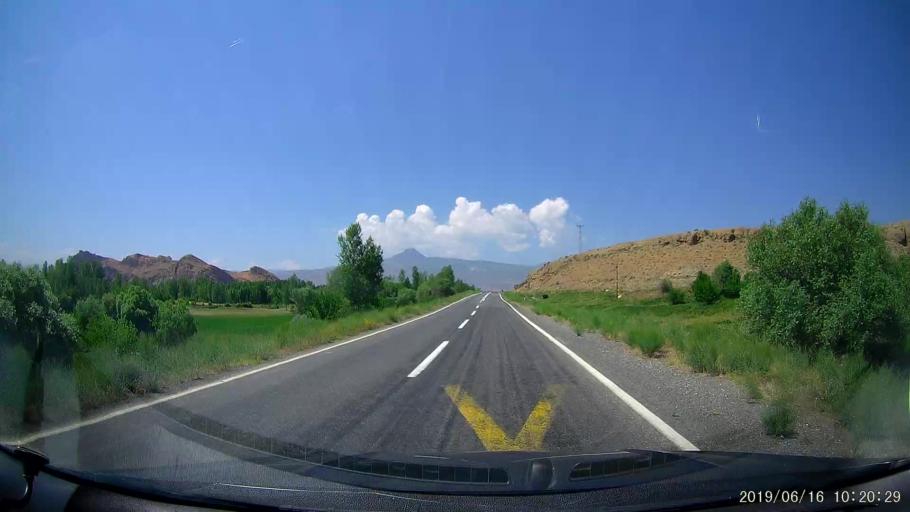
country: TR
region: Igdir
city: Tuzluca
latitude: 40.1473
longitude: 43.6472
